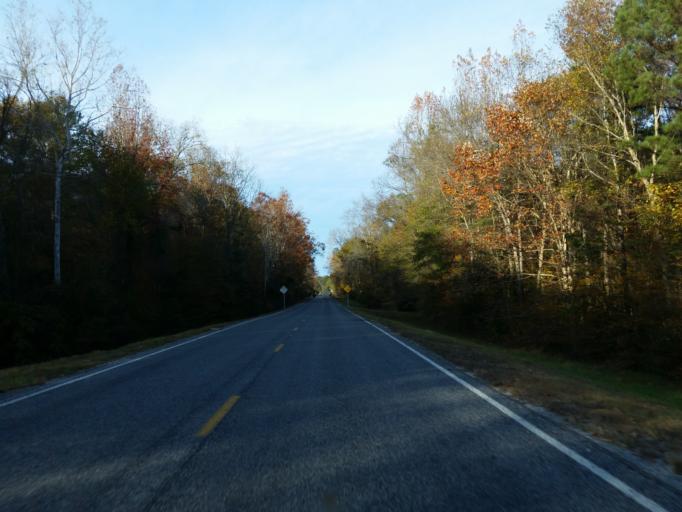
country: US
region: Mississippi
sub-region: Clarke County
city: Stonewall
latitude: 32.0601
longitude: -88.8805
